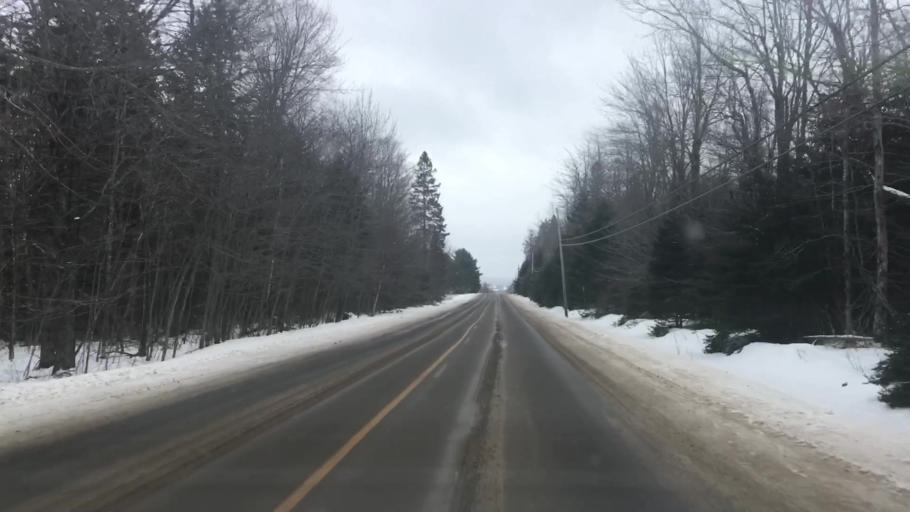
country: US
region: Maine
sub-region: Washington County
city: East Machias
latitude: 44.9835
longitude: -67.4558
